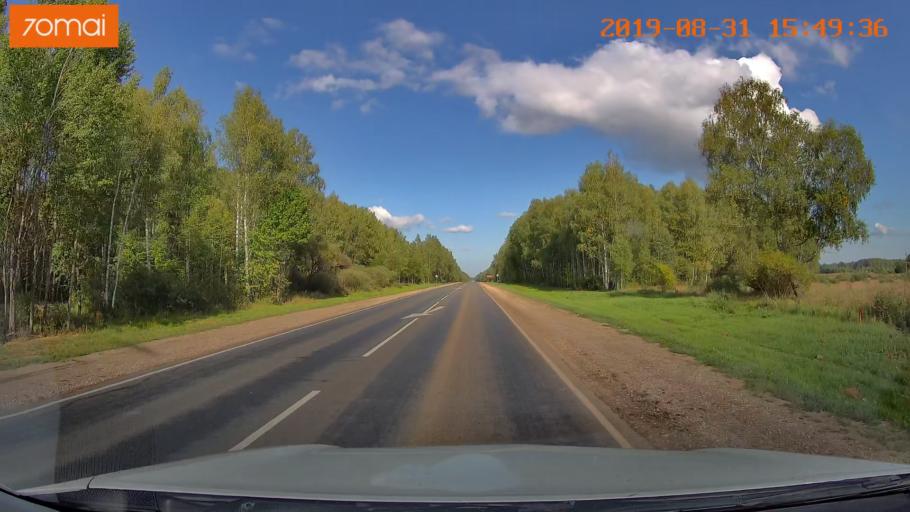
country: RU
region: Kaluga
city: Yukhnov
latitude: 54.6918
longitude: 35.0533
